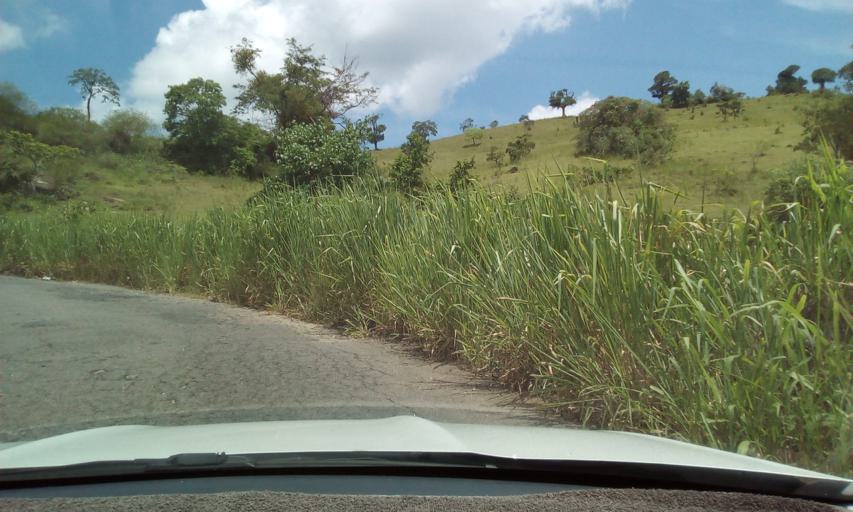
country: BR
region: Pernambuco
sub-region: Bonito
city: Bonito
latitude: -8.4916
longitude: -35.7309
